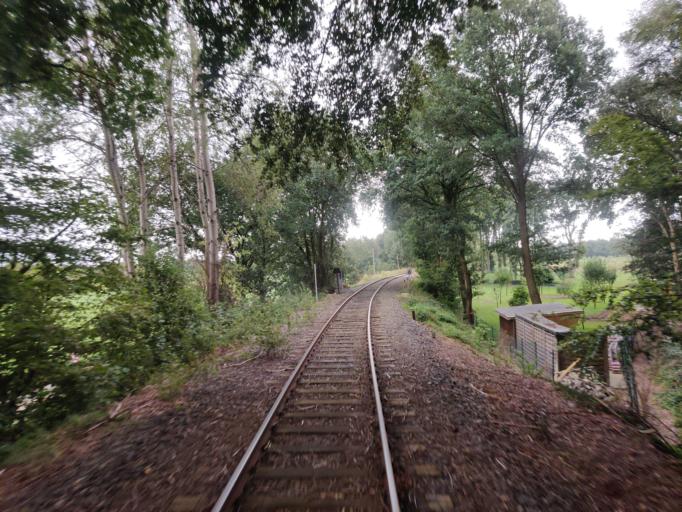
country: DE
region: Lower Saxony
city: Osterholz-Scharmbeck
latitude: 53.2329
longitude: 8.8204
